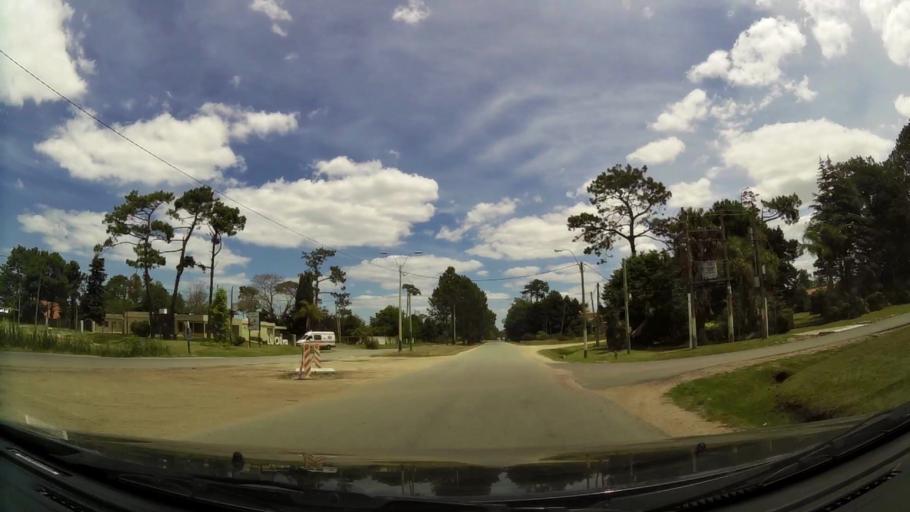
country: UY
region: Canelones
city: Pando
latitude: -34.8011
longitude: -55.8953
